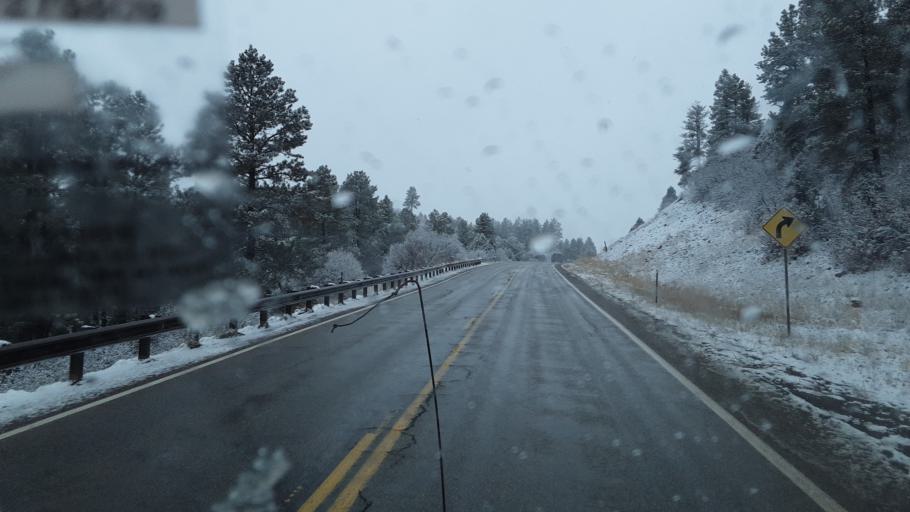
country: US
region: Colorado
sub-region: Archuleta County
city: Pagosa Springs
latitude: 37.2069
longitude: -106.9743
